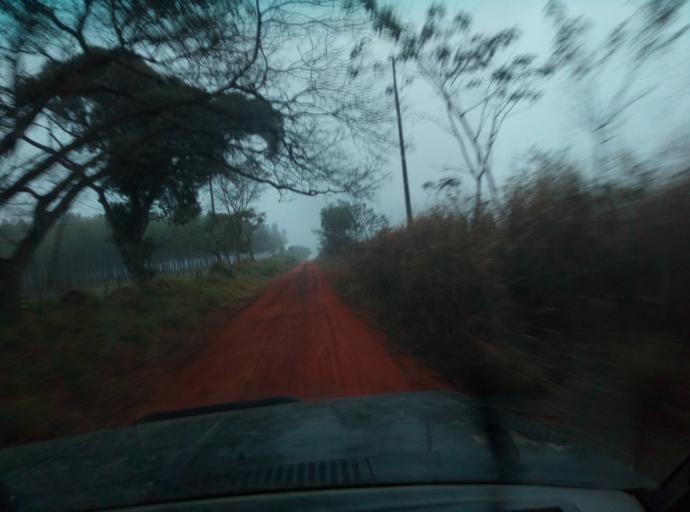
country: PY
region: Caaguazu
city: Doctor Cecilio Baez
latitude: -25.1554
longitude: -56.2855
